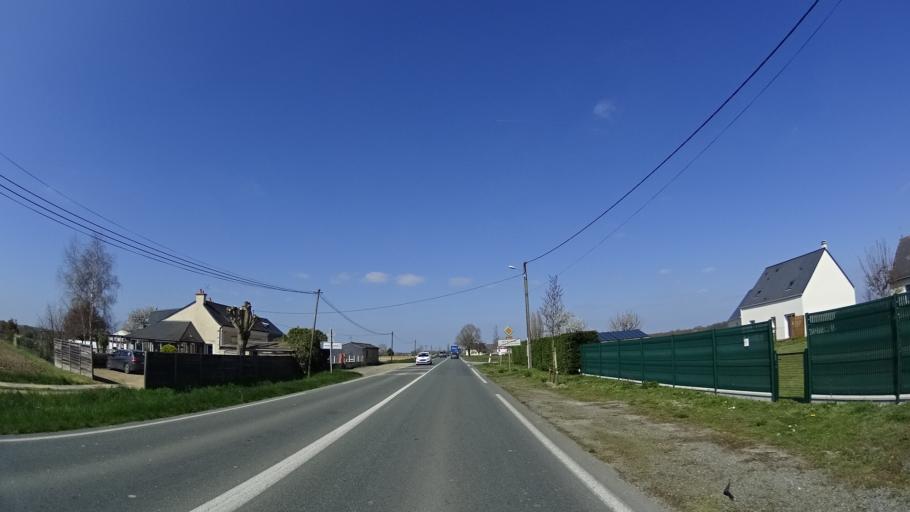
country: FR
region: Pays de la Loire
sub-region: Departement de Maine-et-Loire
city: Brissac-Quince
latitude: 47.3226
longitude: -0.4128
